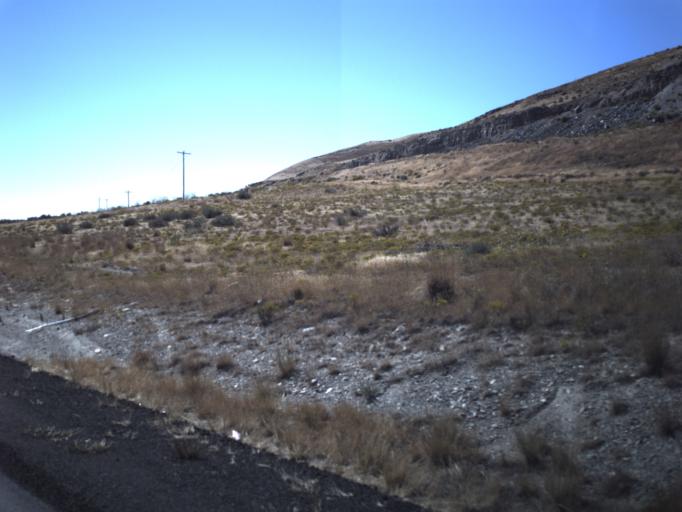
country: US
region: Utah
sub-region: Utah County
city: Saratoga Springs
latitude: 40.2522
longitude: -111.8666
